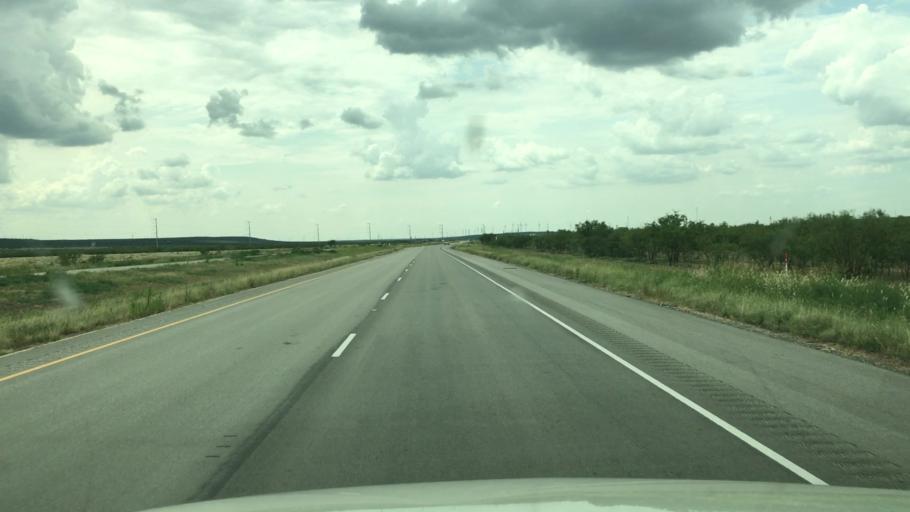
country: US
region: Texas
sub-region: Sterling County
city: Sterling City
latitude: 31.9626
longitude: -101.2188
